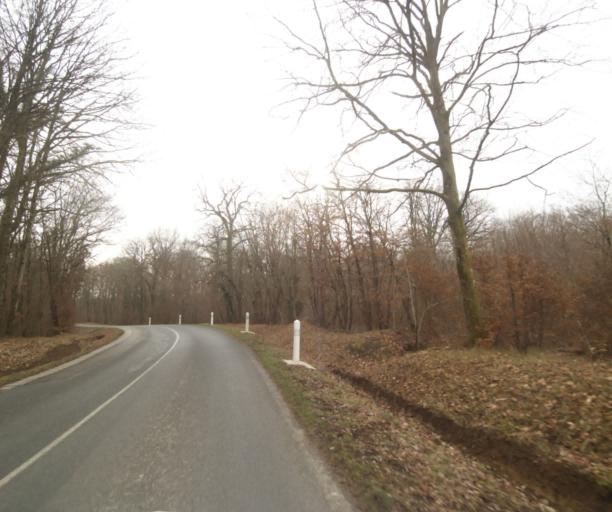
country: FR
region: Champagne-Ardenne
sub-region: Departement de la Marne
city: Pargny-sur-Saulx
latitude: 48.7293
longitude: 4.8666
